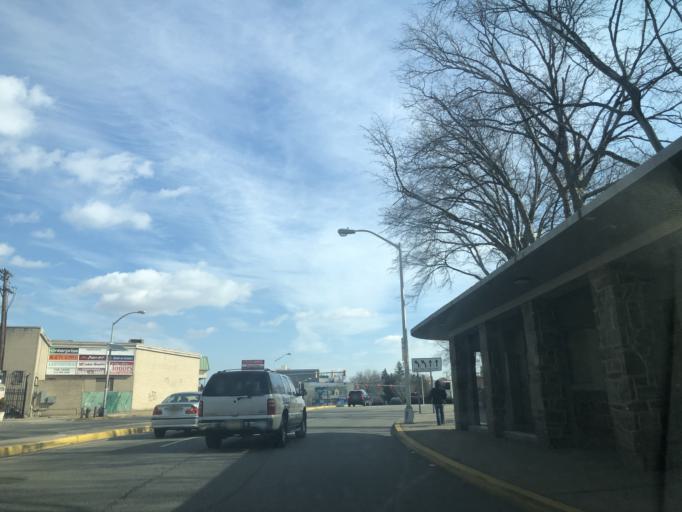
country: US
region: New Jersey
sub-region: Hudson County
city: Bayonne
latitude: 40.6925
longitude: -74.1029
